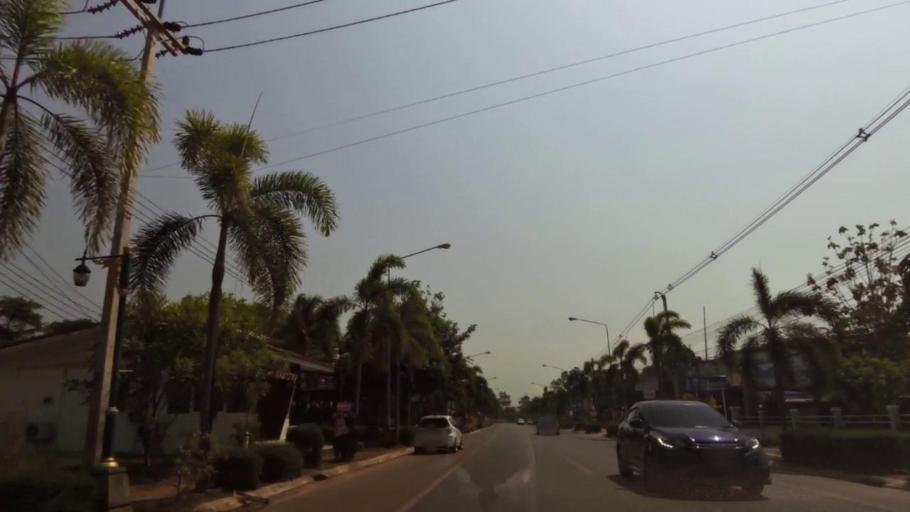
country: TH
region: Chanthaburi
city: Tha Mai
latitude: 12.5518
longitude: 101.9237
